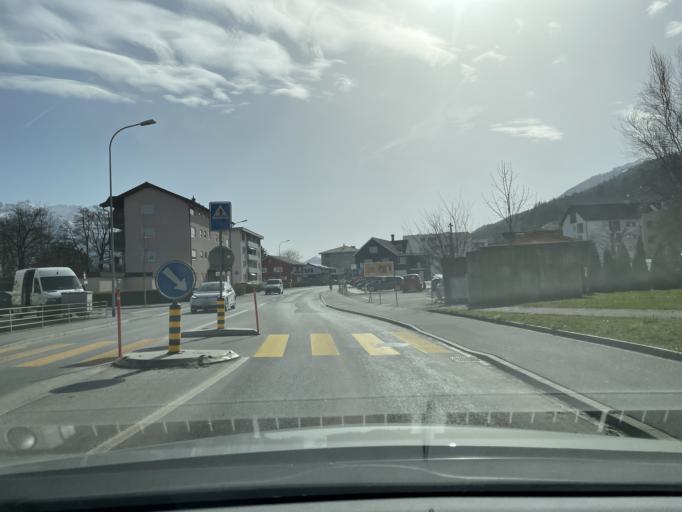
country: CH
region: Saint Gallen
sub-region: Wahlkreis Werdenberg
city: Buchs
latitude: 47.1553
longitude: 9.4804
